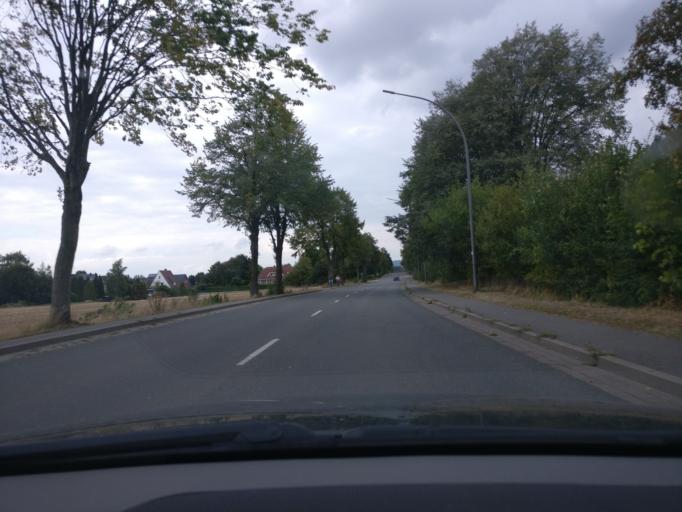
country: DE
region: Lower Saxony
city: Melle
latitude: 52.1895
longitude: 8.3372
